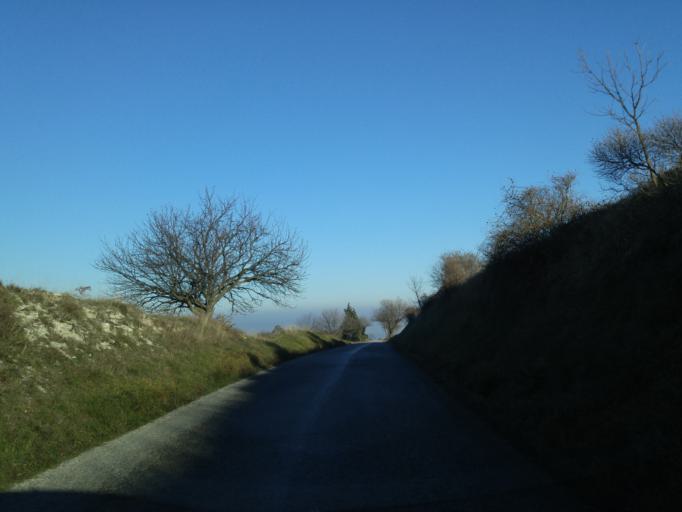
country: IT
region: The Marches
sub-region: Provincia di Pesaro e Urbino
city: Isola del Piano
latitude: 43.7134
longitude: 12.7426
